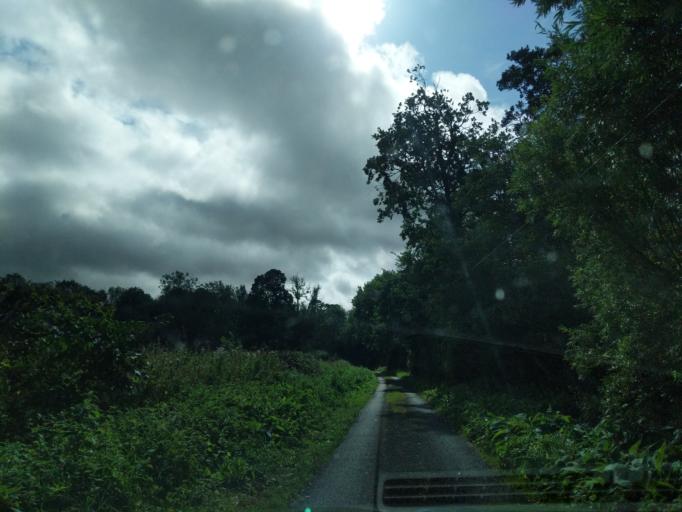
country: GB
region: Scotland
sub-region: The Scottish Borders
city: Kelso
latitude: 55.5686
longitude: -2.4725
